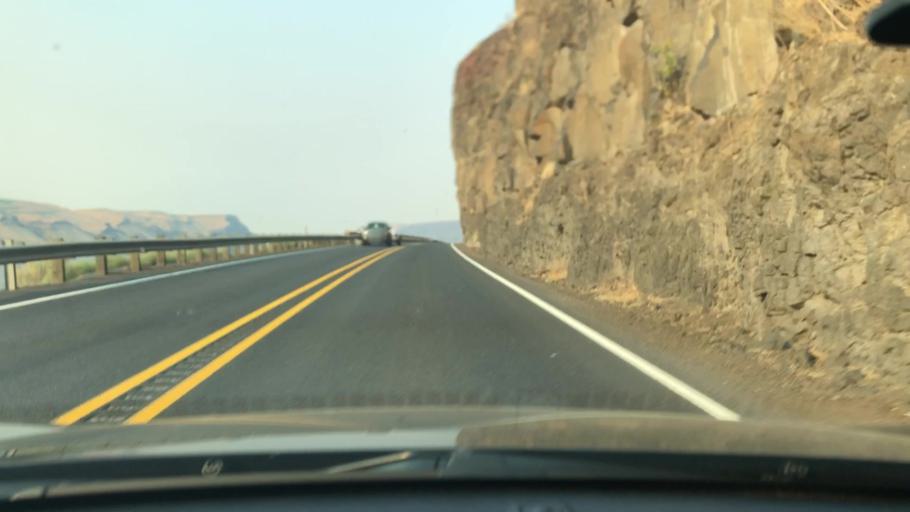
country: US
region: Washington
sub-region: Benton County
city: Highland
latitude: 45.9495
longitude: -119.0616
